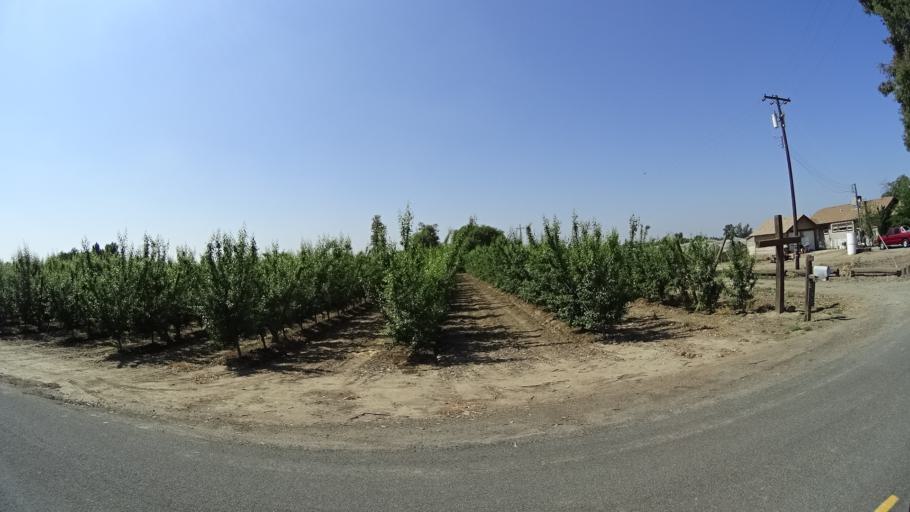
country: US
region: California
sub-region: Fresno County
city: Kingsburg
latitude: 36.4524
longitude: -119.5574
